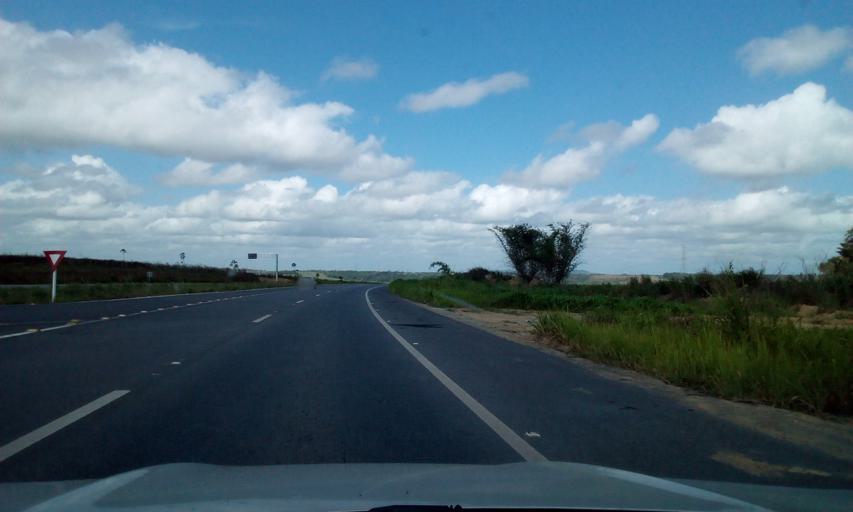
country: BR
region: Alagoas
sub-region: Rio Largo
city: Rio Largo
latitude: -9.4538
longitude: -35.8749
